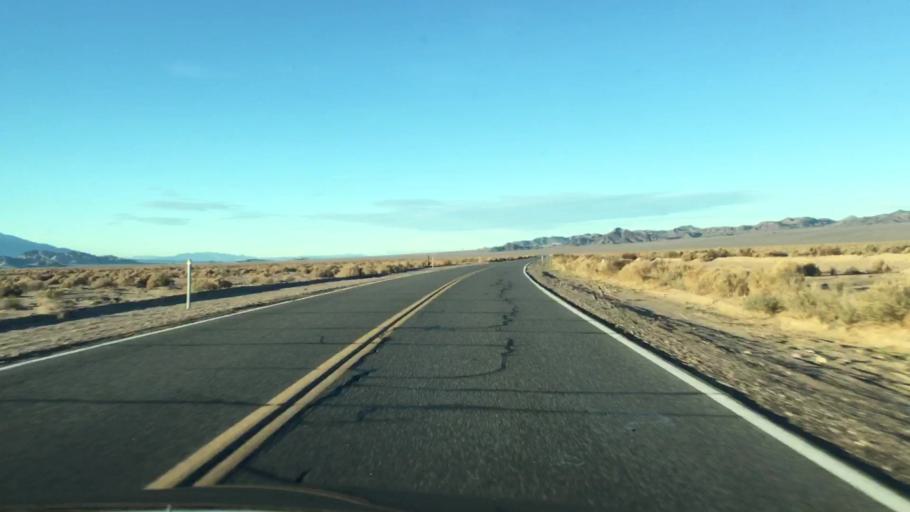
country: US
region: California
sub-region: San Bernardino County
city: Fort Irwin
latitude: 35.2951
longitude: -116.0826
